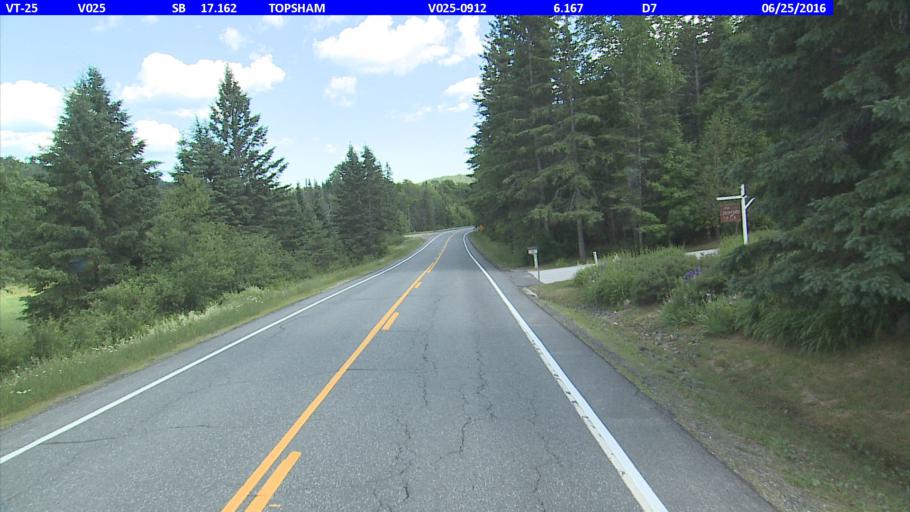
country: US
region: Vermont
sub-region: Orange County
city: Chelsea
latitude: 44.1334
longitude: -72.3154
